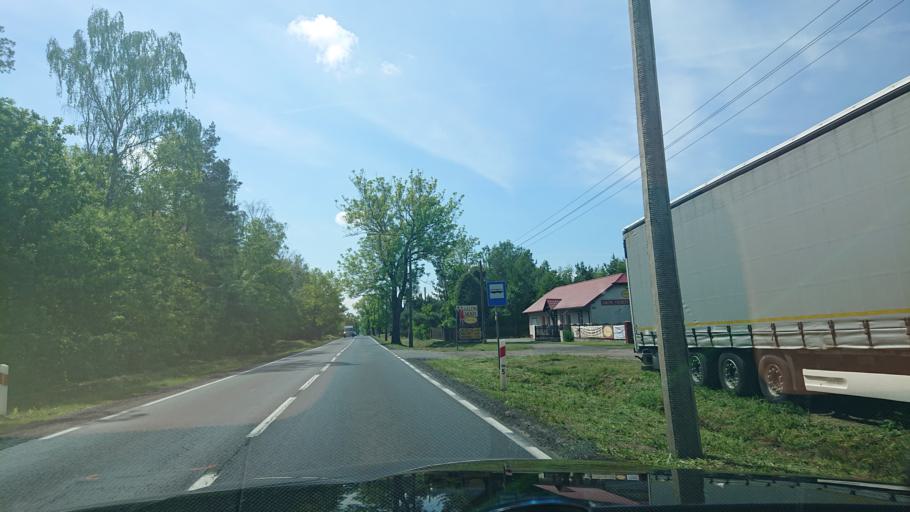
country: PL
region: Greater Poland Voivodeship
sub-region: Powiat gnieznienski
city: Gniezno
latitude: 52.4984
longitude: 17.5943
